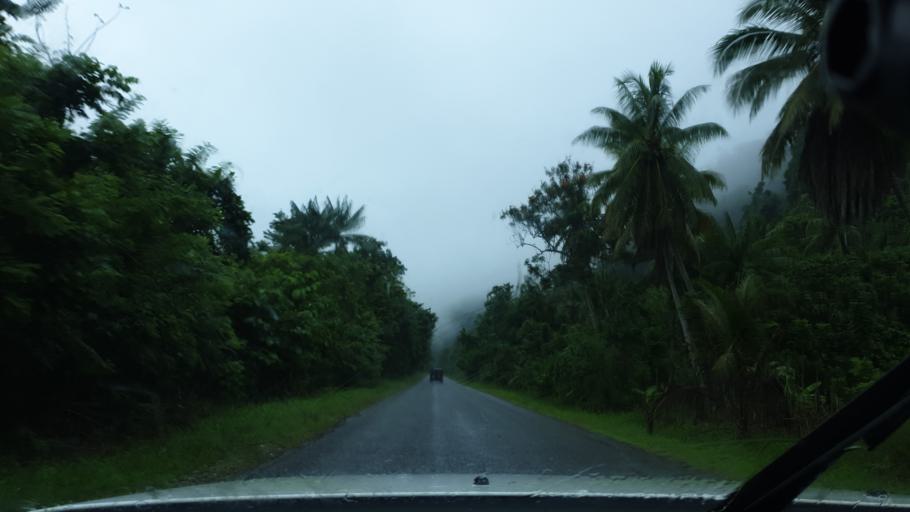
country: PG
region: Madang
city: Madang
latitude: -5.3262
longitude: 145.7171
